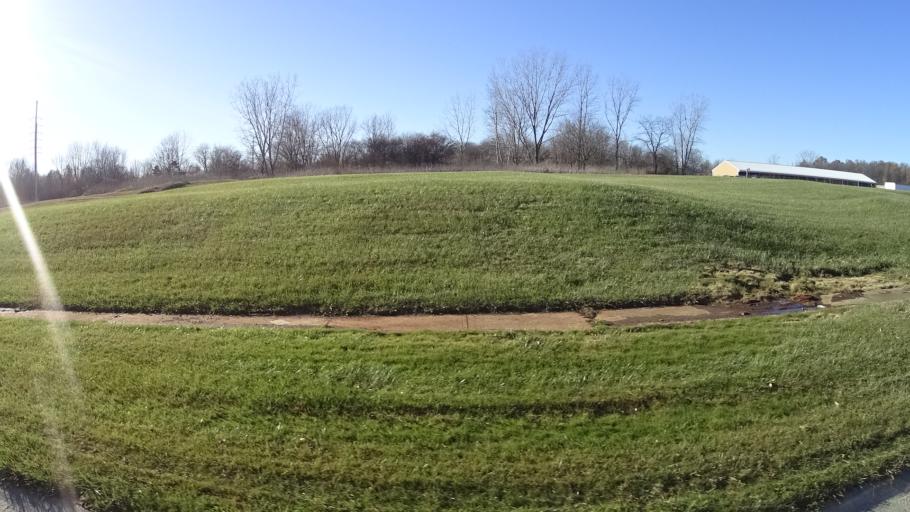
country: US
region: Ohio
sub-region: Lorain County
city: Elyria
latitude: 41.3587
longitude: -82.1237
